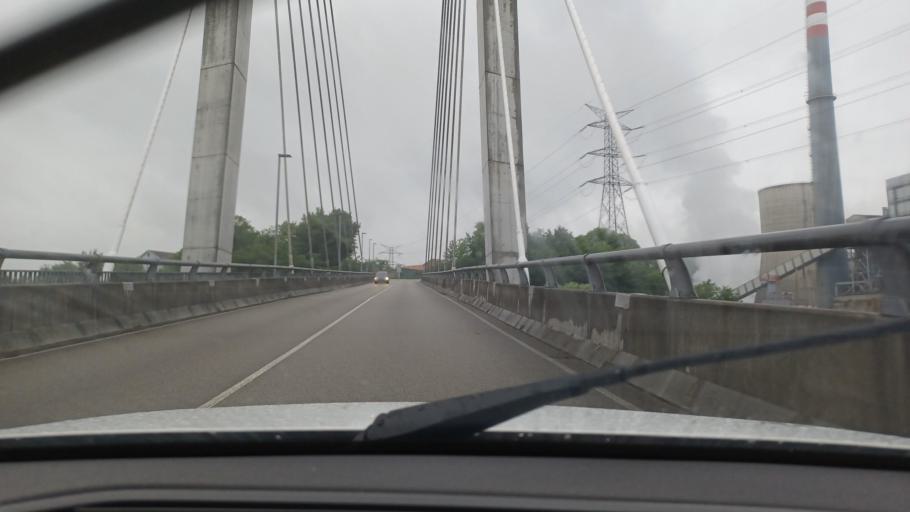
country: ES
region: Asturias
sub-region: Province of Asturias
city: Castandiello
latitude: 43.3099
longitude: -5.8729
